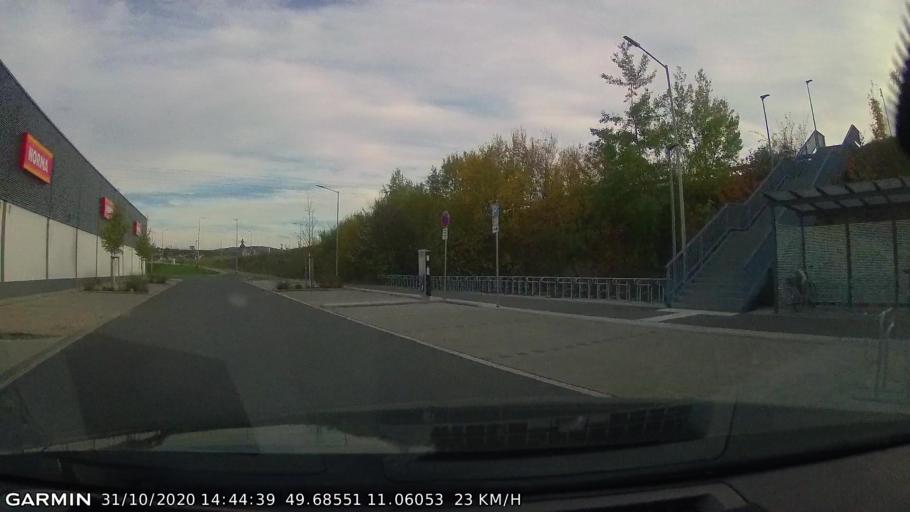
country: DE
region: Bavaria
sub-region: Upper Franconia
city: Poxdorf
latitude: 49.6853
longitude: 11.0610
